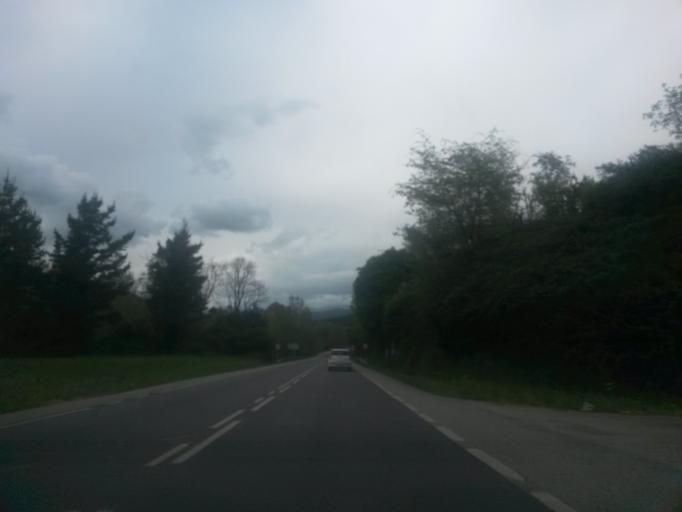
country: ES
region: Catalonia
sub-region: Provincia de Girona
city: Angles
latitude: 41.9470
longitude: 2.6417
